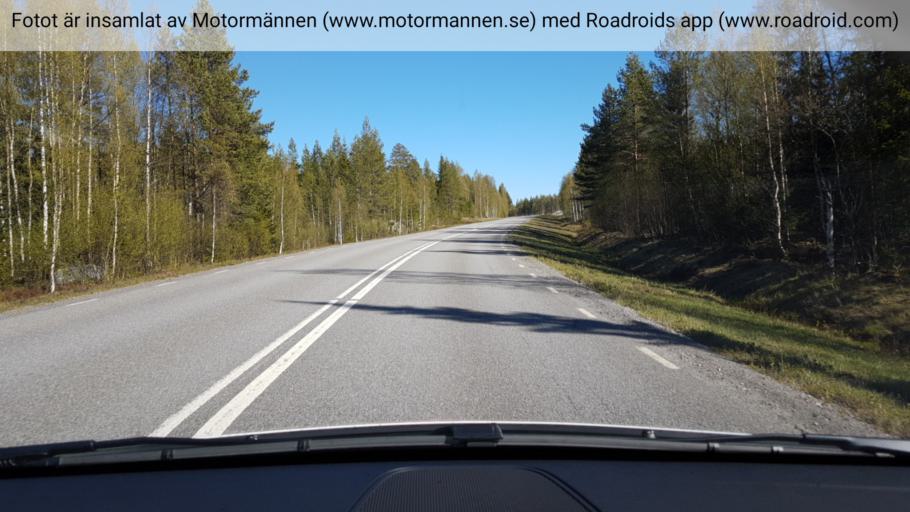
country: SE
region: Jaemtland
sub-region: Stroemsunds Kommun
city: Stroemsund
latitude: 64.3263
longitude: 15.1876
